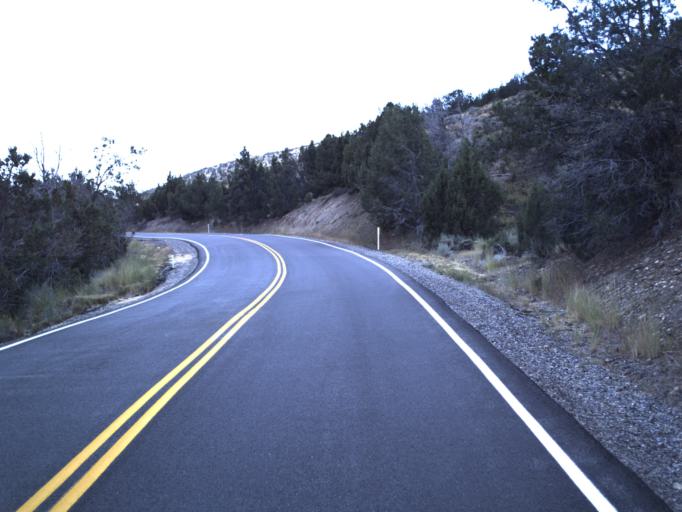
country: US
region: Utah
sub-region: Tooele County
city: Grantsville
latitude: 40.3404
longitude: -112.5676
